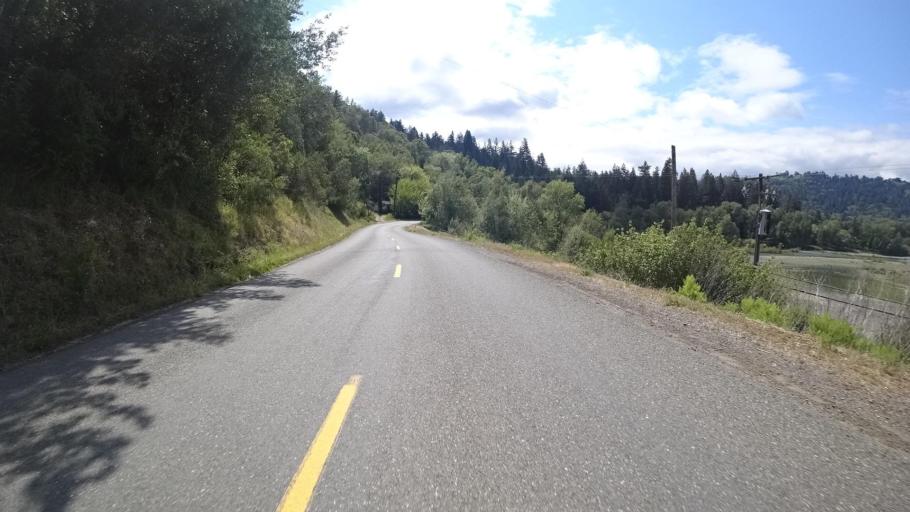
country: US
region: California
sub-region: Humboldt County
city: Redway
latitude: 40.0940
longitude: -123.7956
